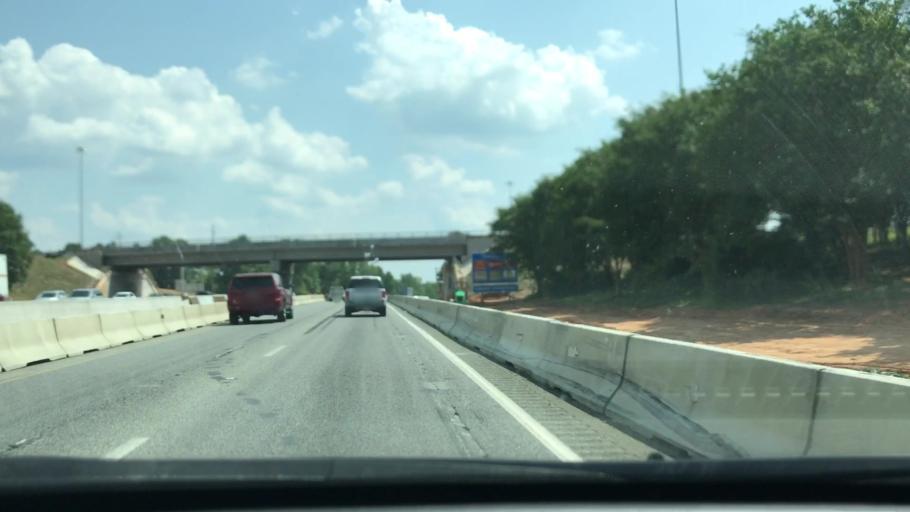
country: US
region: North Carolina
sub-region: Mecklenburg County
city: Cornelius
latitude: 35.5050
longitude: -80.8664
